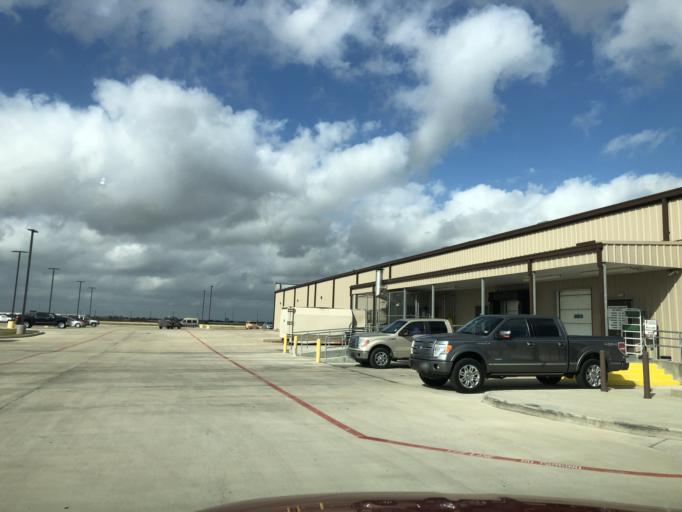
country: US
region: Texas
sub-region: Austin County
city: Sealy
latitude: 29.7615
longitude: -96.1867
